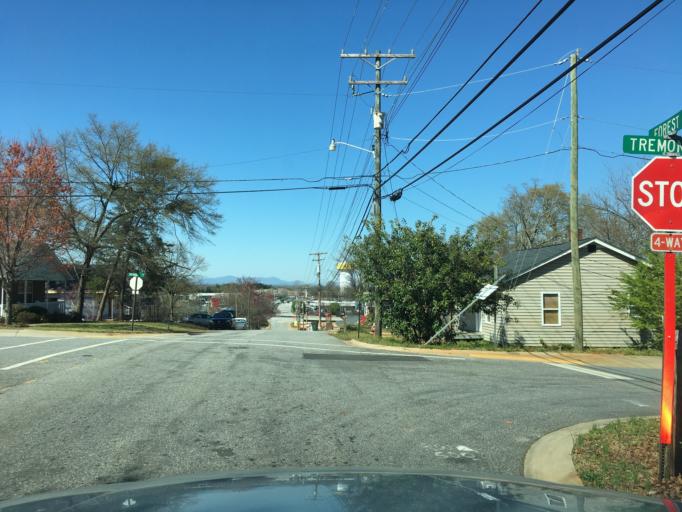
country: US
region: South Carolina
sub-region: Greenville County
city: Greer
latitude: 34.9459
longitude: -82.2379
